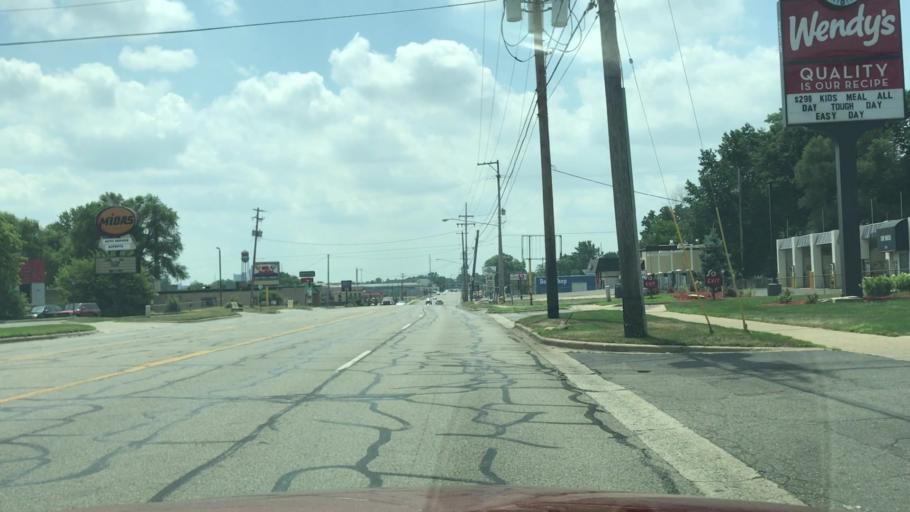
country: US
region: Michigan
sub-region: Kent County
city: Comstock Park
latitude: 43.0060
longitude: -85.6887
